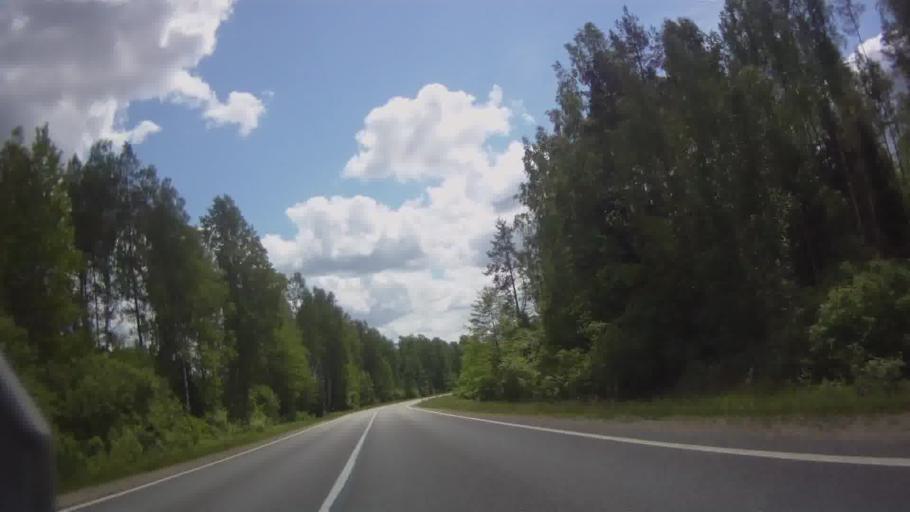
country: LV
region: Livani
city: Livani
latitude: 56.5354
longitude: 26.1372
